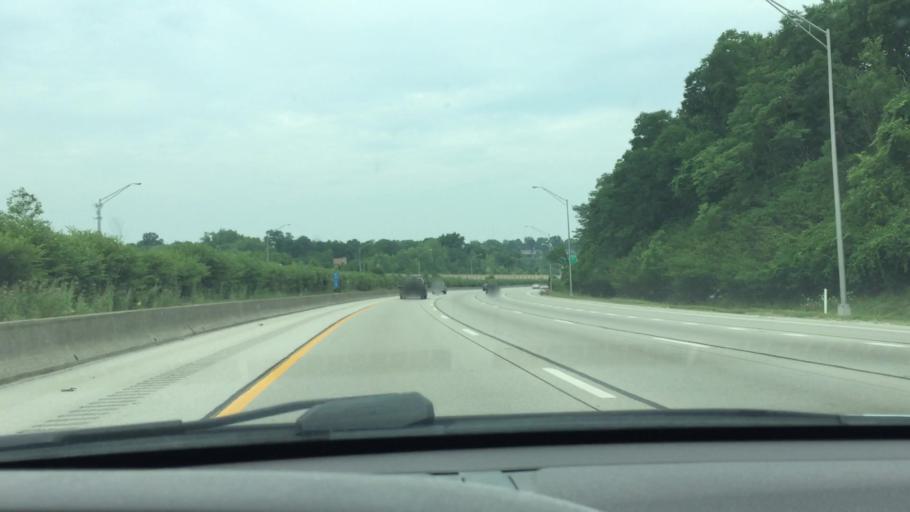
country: US
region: Kentucky
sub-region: Campbell County
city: Southgate
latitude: 39.0753
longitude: -84.4674
